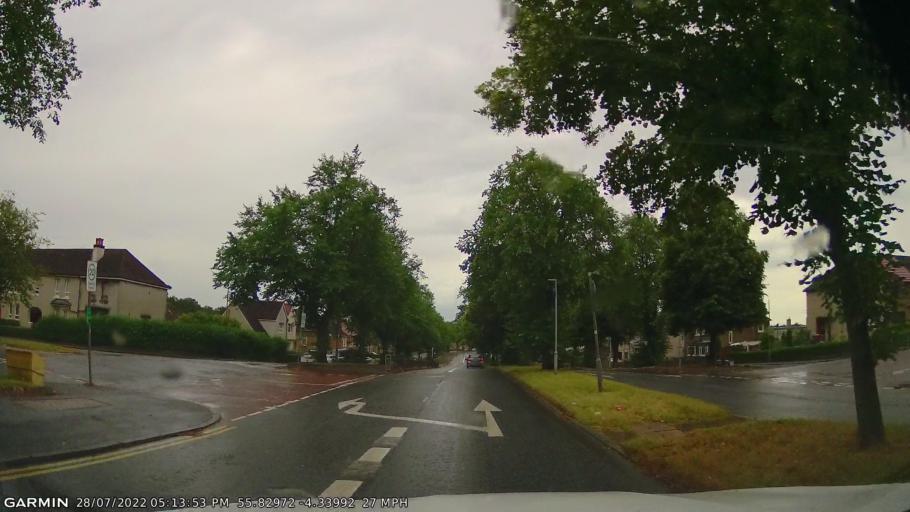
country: GB
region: Scotland
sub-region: East Renfrewshire
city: Giffnock
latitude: 55.8297
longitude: -4.3399
